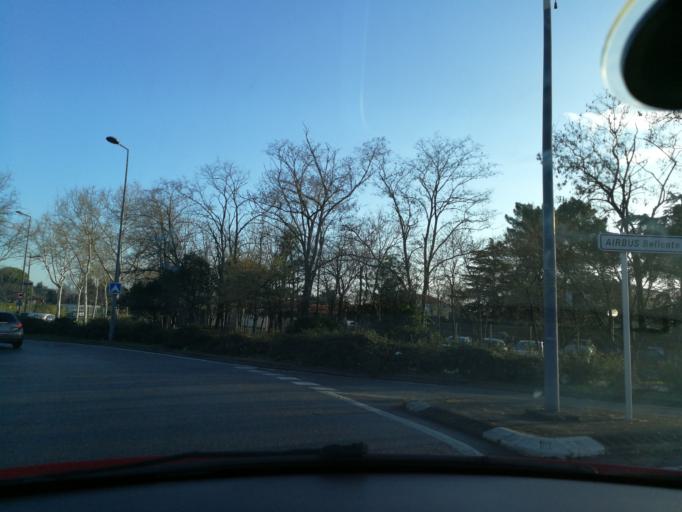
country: FR
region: Midi-Pyrenees
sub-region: Departement de la Haute-Garonne
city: Blagnac
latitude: 43.6267
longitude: 1.3854
